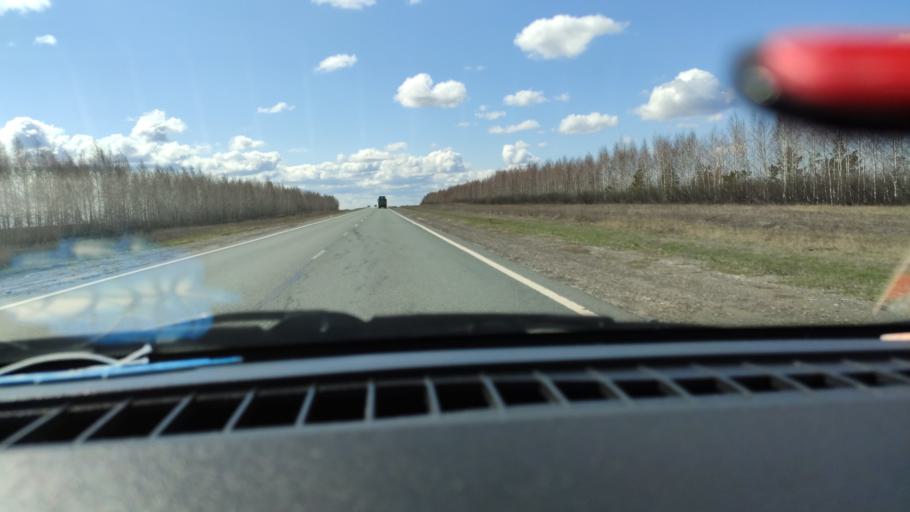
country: RU
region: Saratov
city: Dukhovnitskoye
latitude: 52.8119
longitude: 48.2298
